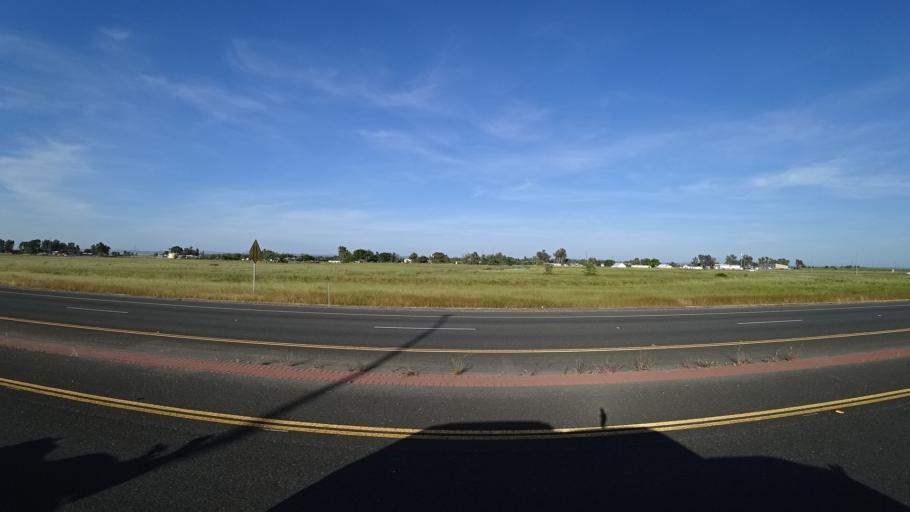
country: US
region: California
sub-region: Placer County
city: Sheridan
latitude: 38.9807
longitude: -121.3835
